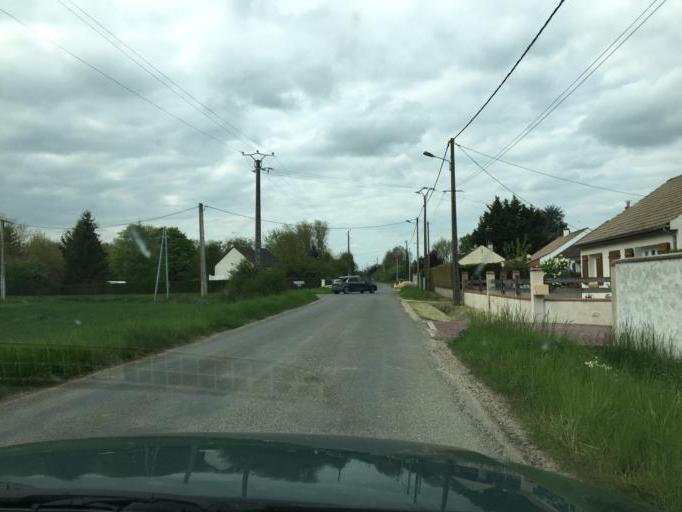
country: FR
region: Centre
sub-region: Departement du Loiret
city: Huisseau-sur-Mauves
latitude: 47.8645
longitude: 1.6953
